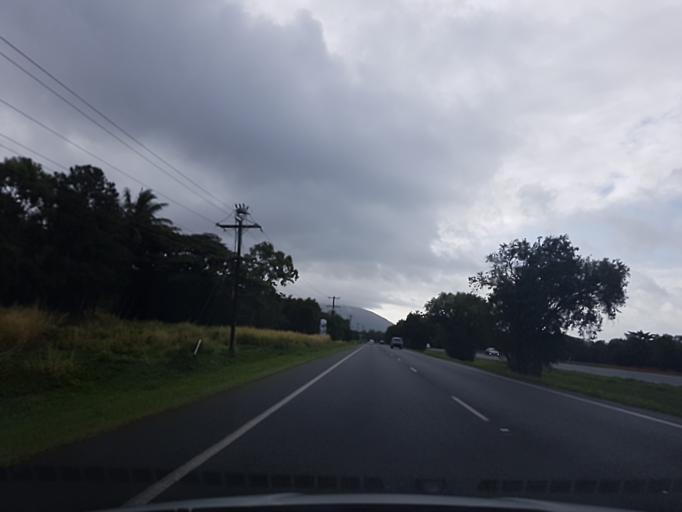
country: AU
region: Queensland
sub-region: Cairns
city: Trinity Beach
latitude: -16.8039
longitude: 145.6895
